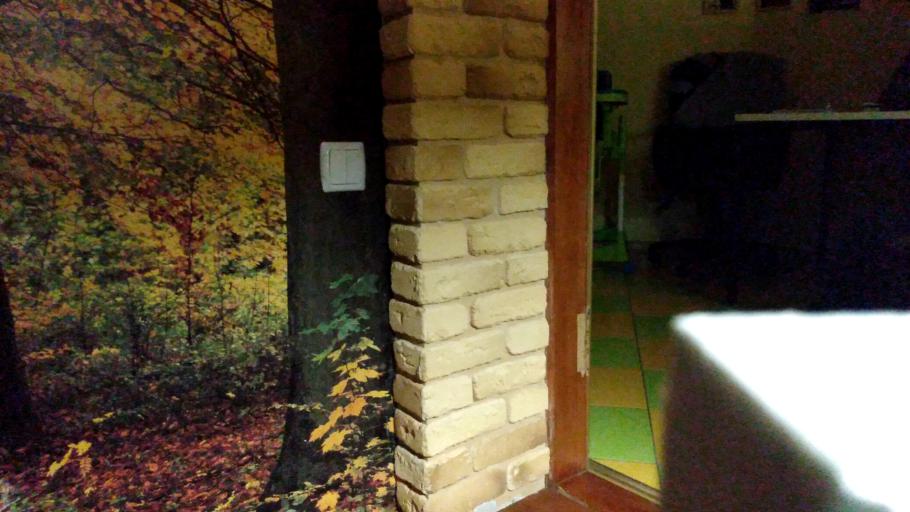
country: RU
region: Vologda
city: Lipin Bor
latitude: 60.7698
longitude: 38.0440
